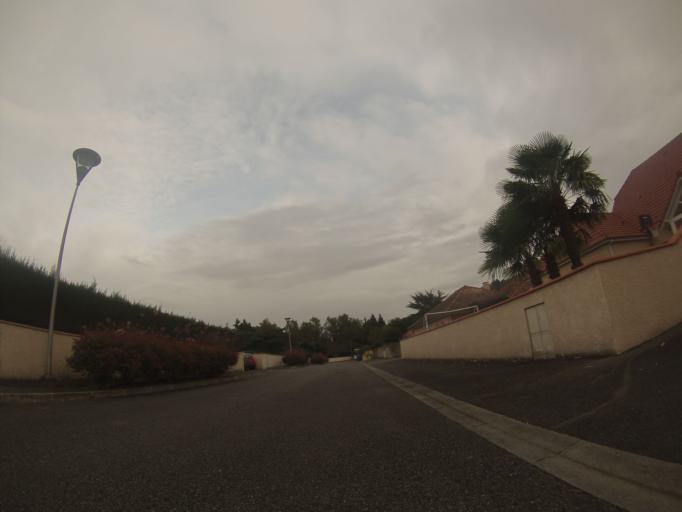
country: FR
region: Aquitaine
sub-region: Departement des Pyrenees-Atlantiques
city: Bizanos
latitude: 43.2751
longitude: -0.3544
